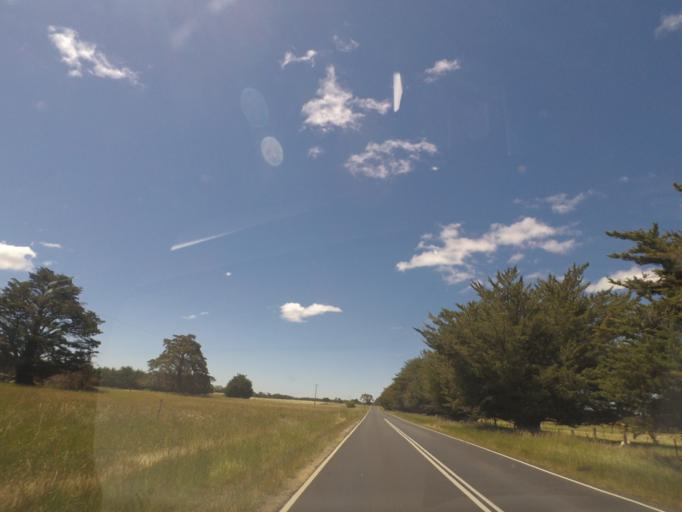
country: AU
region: Victoria
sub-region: Mount Alexander
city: Castlemaine
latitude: -37.2499
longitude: 144.3203
